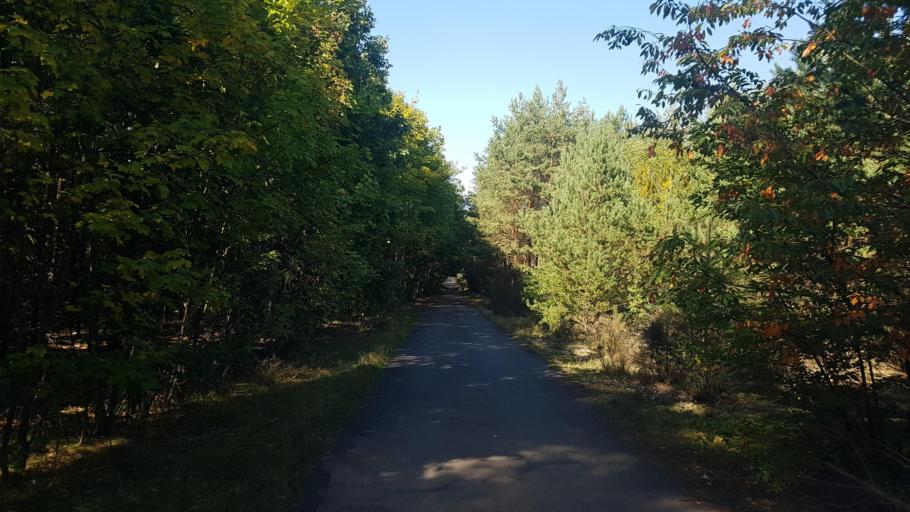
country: DE
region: Brandenburg
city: Ihlow
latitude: 51.8610
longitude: 13.2589
